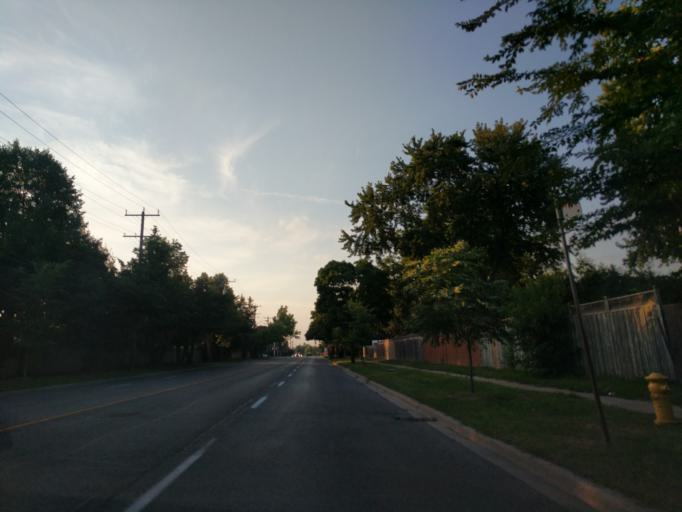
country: CA
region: Ontario
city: Scarborough
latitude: 43.7950
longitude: -79.3042
